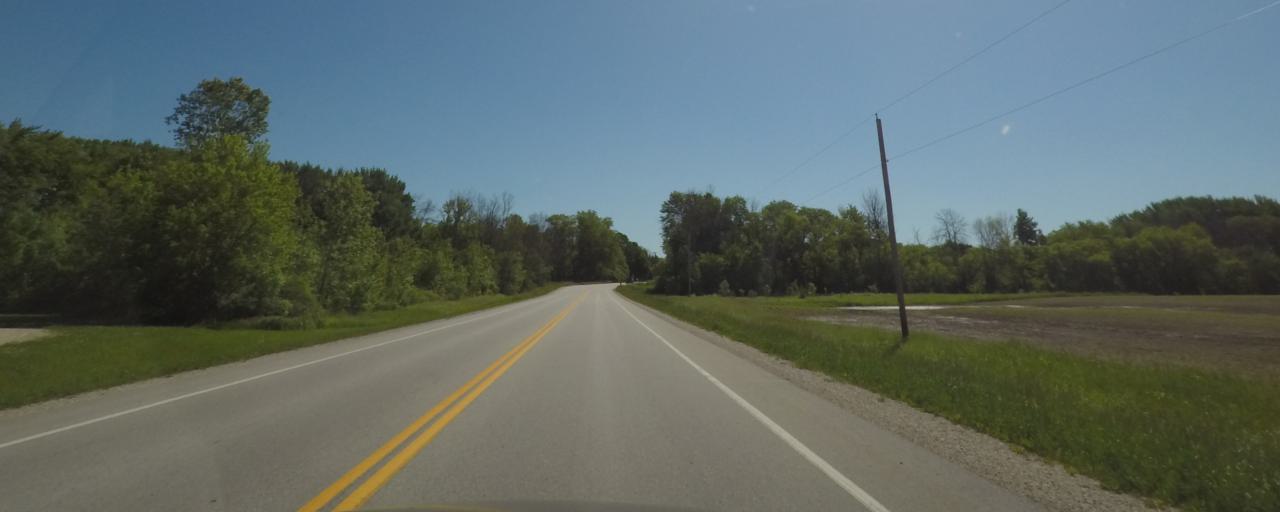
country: US
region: Wisconsin
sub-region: Sheboygan County
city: Plymouth
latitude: 43.7465
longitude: -87.9142
